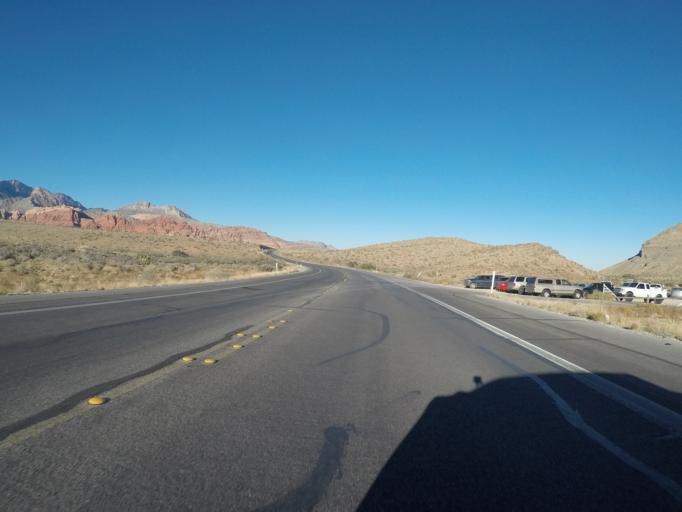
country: US
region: Nevada
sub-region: Clark County
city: Summerlin South
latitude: 36.1214
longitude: -115.4343
